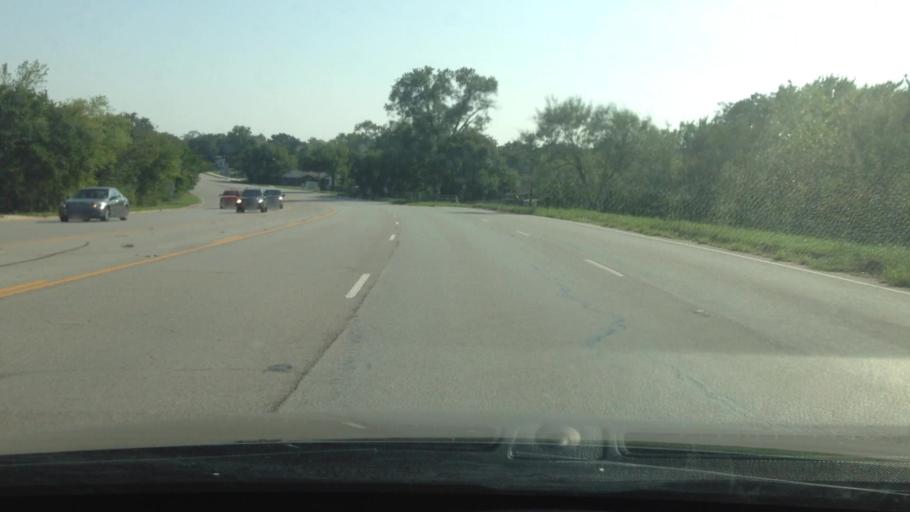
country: US
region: Texas
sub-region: Tarrant County
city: North Richland Hills
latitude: 32.8758
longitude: -97.2056
